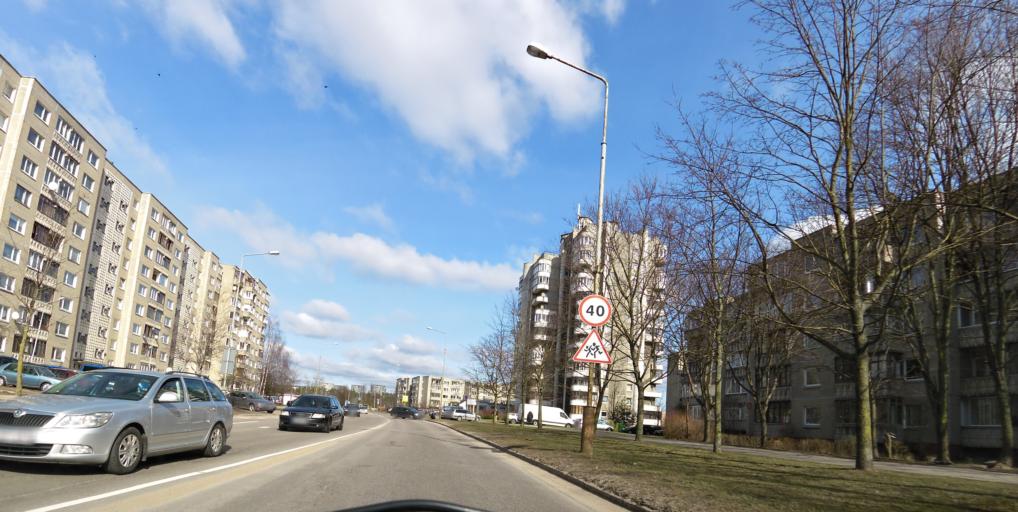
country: LT
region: Vilnius County
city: Seskine
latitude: 54.7164
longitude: 25.2578
